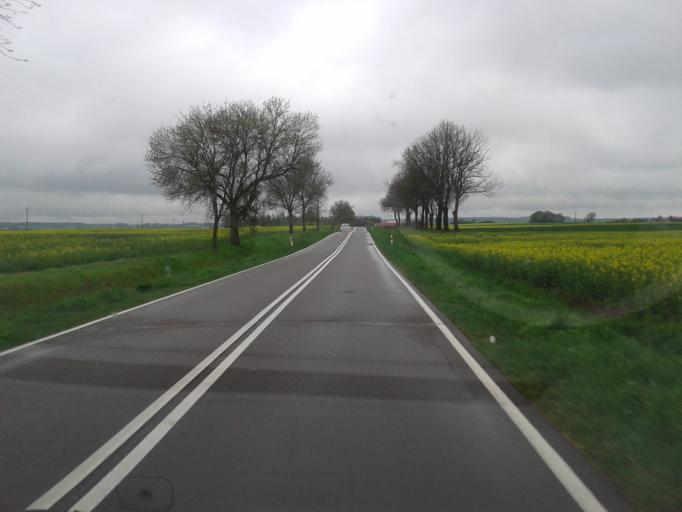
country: PL
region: Lublin Voivodeship
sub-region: Powiat tomaszowski
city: Telatyn
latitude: 50.5475
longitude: 23.9287
